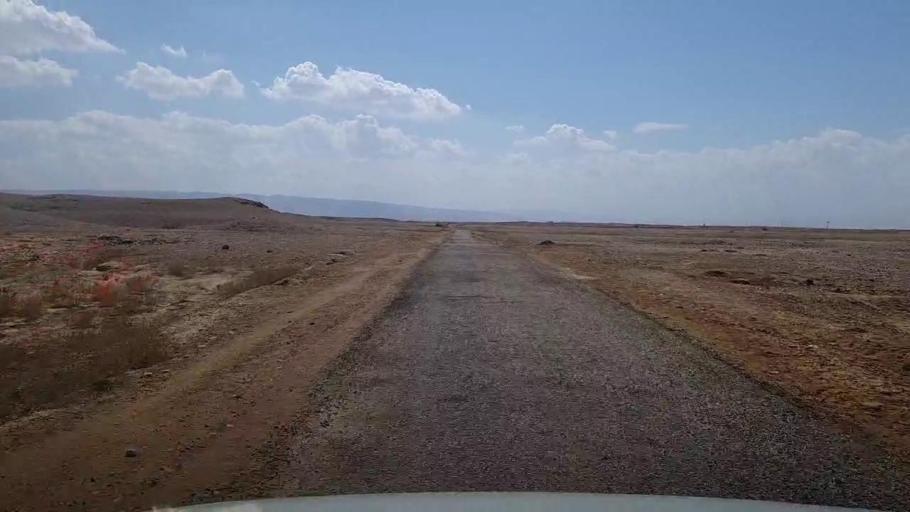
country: PK
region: Sindh
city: Bhan
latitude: 26.3802
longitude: 67.6388
